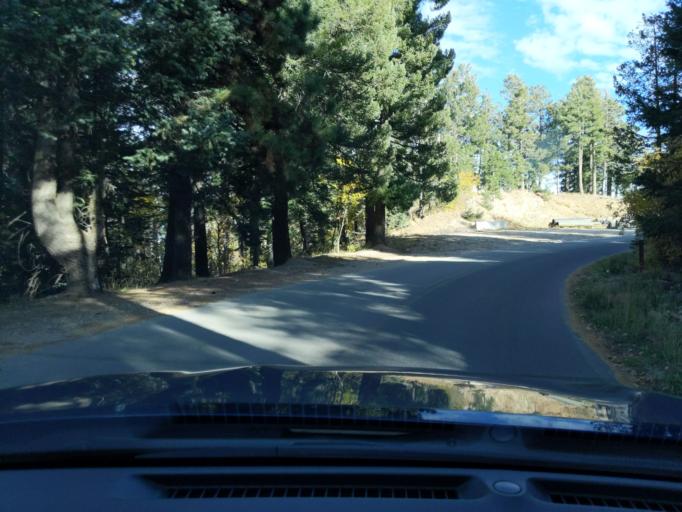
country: US
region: Arizona
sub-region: Pima County
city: Catalina
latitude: 32.4415
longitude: -110.7845
